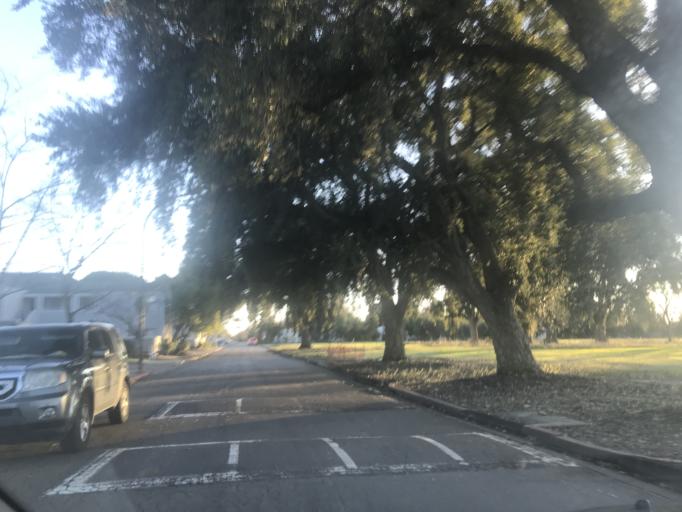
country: US
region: California
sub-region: Yolo County
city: Davis
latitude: 38.5452
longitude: -121.7641
